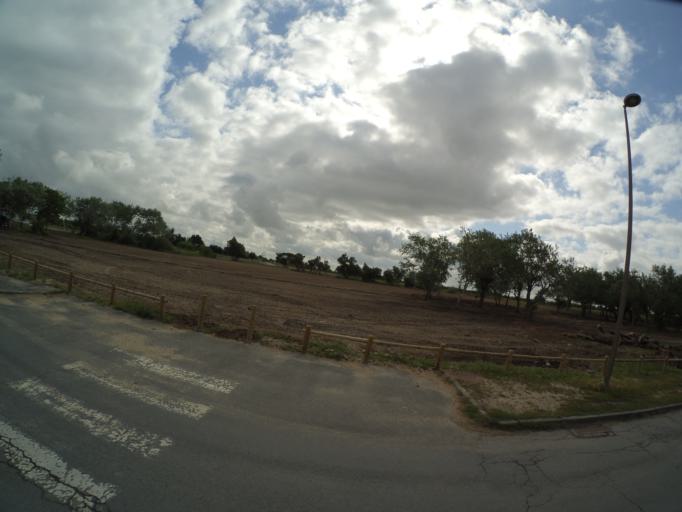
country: FR
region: Poitou-Charentes
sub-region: Departement de la Charente-Maritime
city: Angoulins
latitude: 46.1151
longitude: -1.1233
